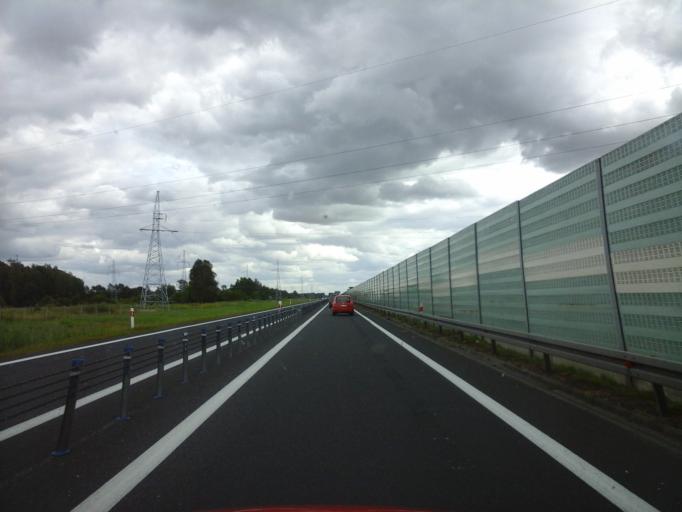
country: PL
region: West Pomeranian Voivodeship
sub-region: Powiat stargardzki
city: Kobylanka
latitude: 53.3604
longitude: 14.9110
